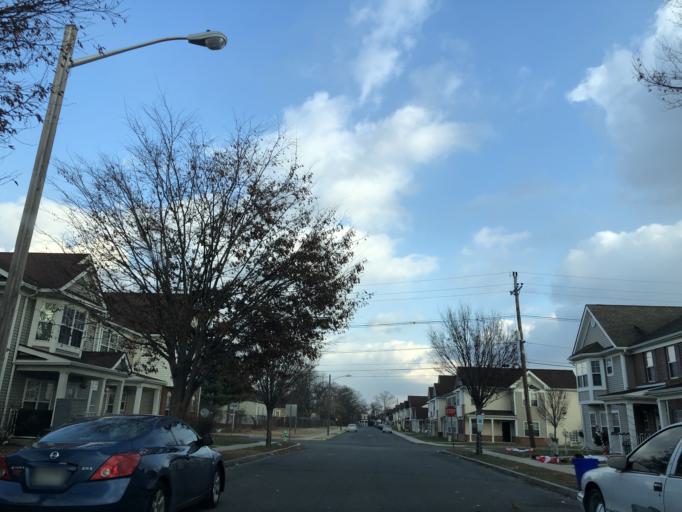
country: US
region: New Jersey
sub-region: Camden County
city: Camden
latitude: 39.9173
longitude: -75.1129
